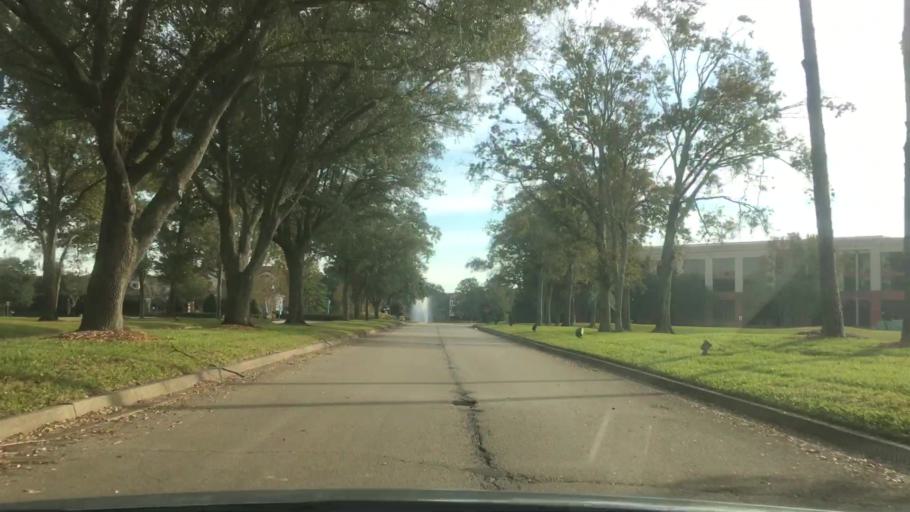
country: US
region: Florida
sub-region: Duval County
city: Jacksonville
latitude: 30.2580
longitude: -81.5990
